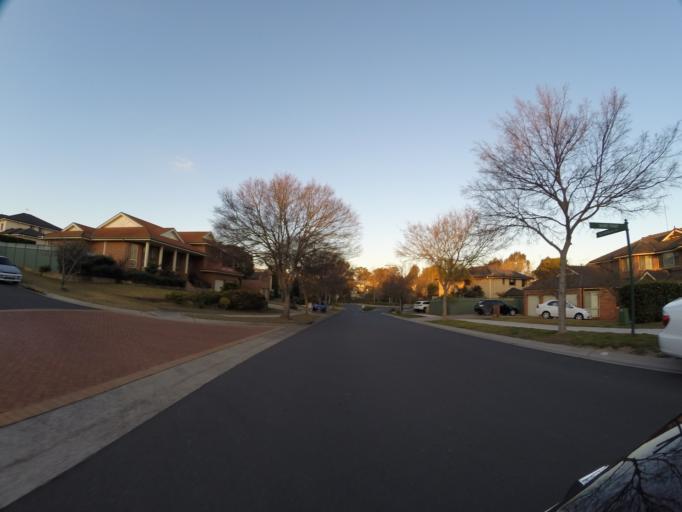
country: AU
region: New South Wales
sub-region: Camden
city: Narellan
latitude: -34.0235
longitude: 150.7372
